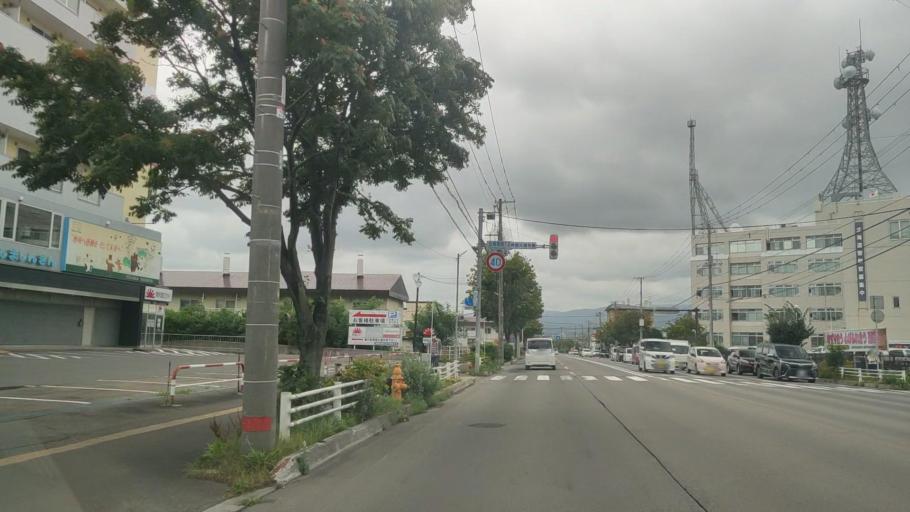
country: JP
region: Hokkaido
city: Hakodate
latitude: 41.7950
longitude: 140.7514
